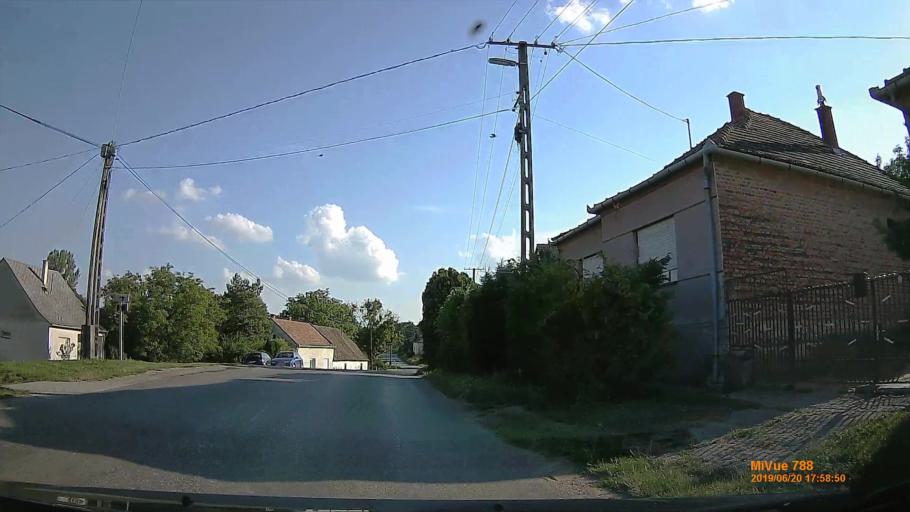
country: HU
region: Baranya
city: Buekkoesd
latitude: 46.1017
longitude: 17.9887
